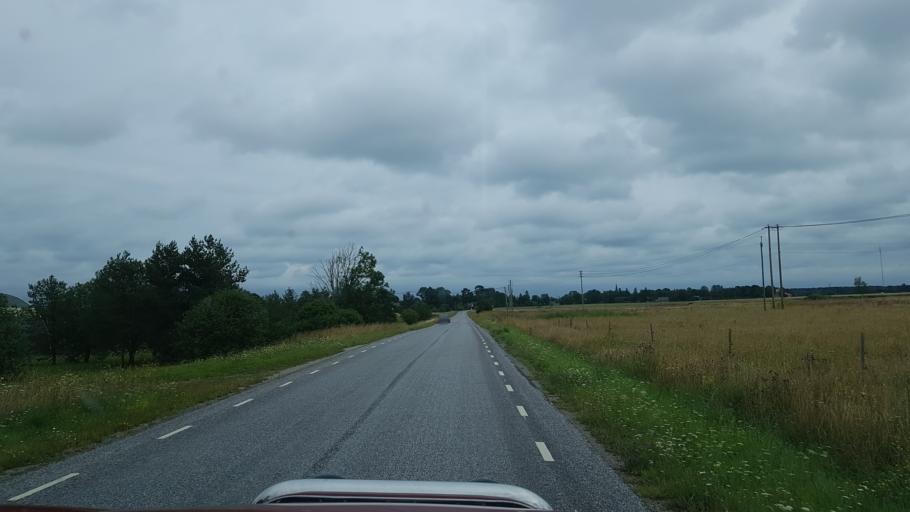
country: EE
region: Ida-Virumaa
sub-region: Puessi linn
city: Pussi
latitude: 59.3895
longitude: 27.0259
